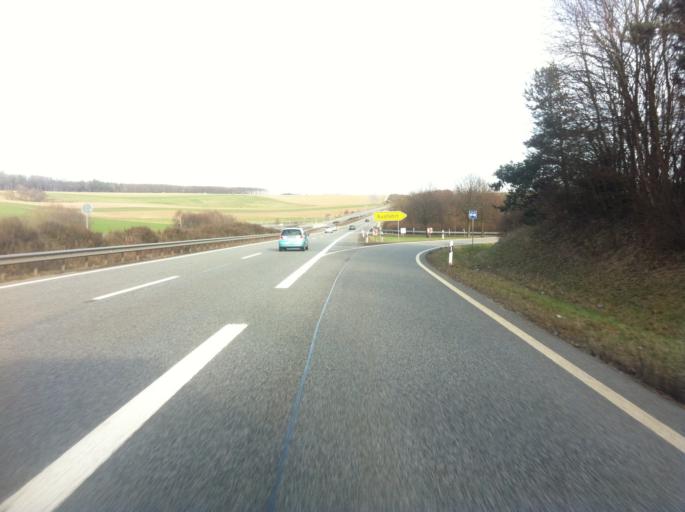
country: DE
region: Rheinland-Pfalz
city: Sohren
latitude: 49.9378
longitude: 7.3061
